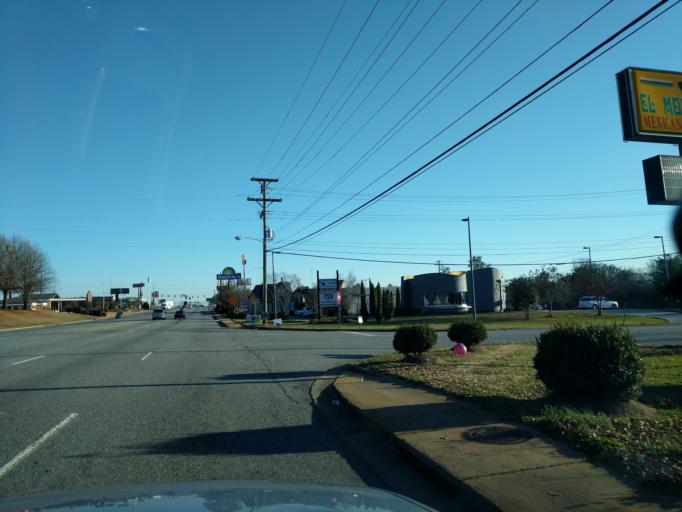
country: US
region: South Carolina
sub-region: Spartanburg County
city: Lyman
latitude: 34.9187
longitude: -82.1131
